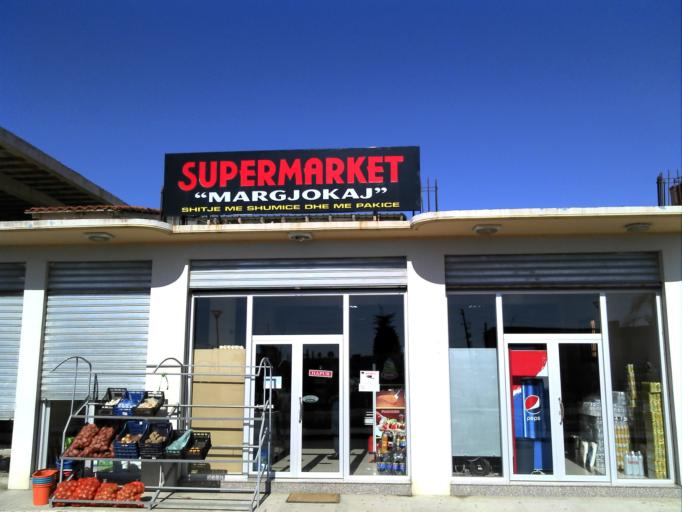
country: AL
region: Shkoder
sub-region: Rrethi i Shkodres
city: Velipoje
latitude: 41.8640
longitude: 19.4229
